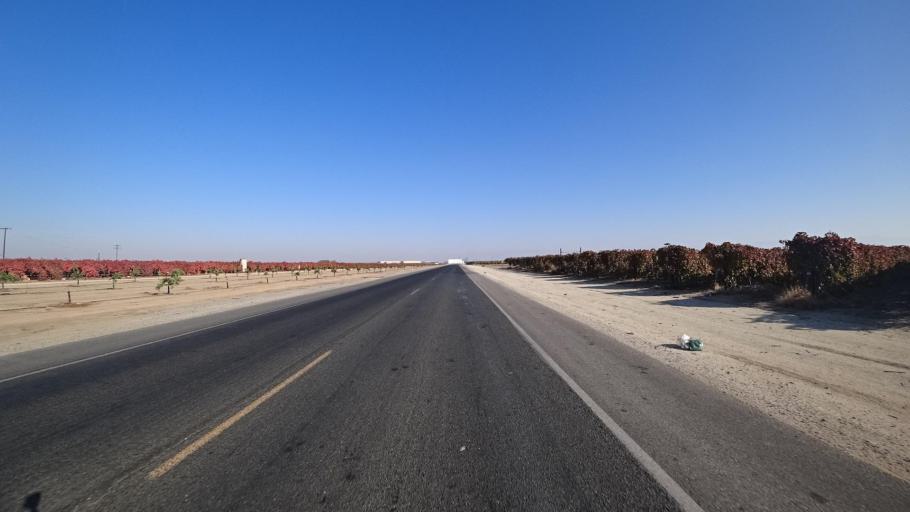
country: US
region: California
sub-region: Tulare County
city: Richgrove
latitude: 35.7354
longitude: -119.1489
